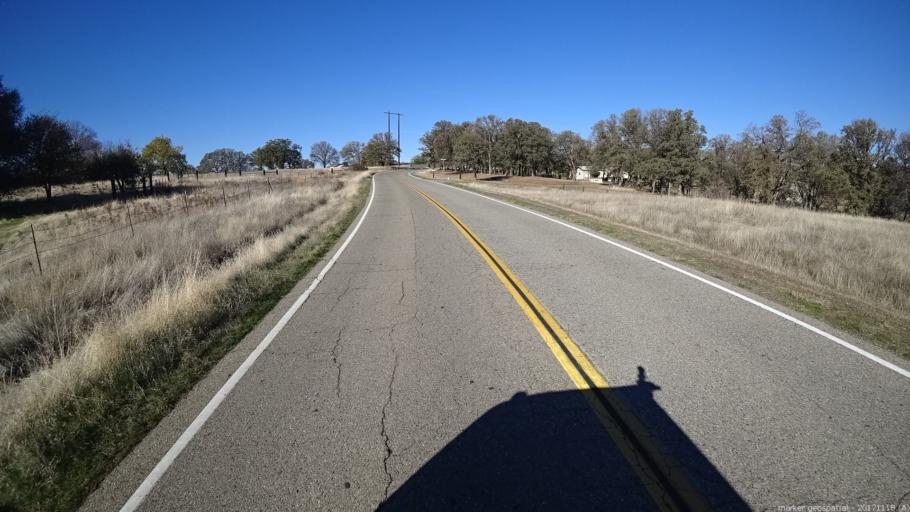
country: US
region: California
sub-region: Shasta County
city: Cottonwood
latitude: 40.3926
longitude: -122.3128
